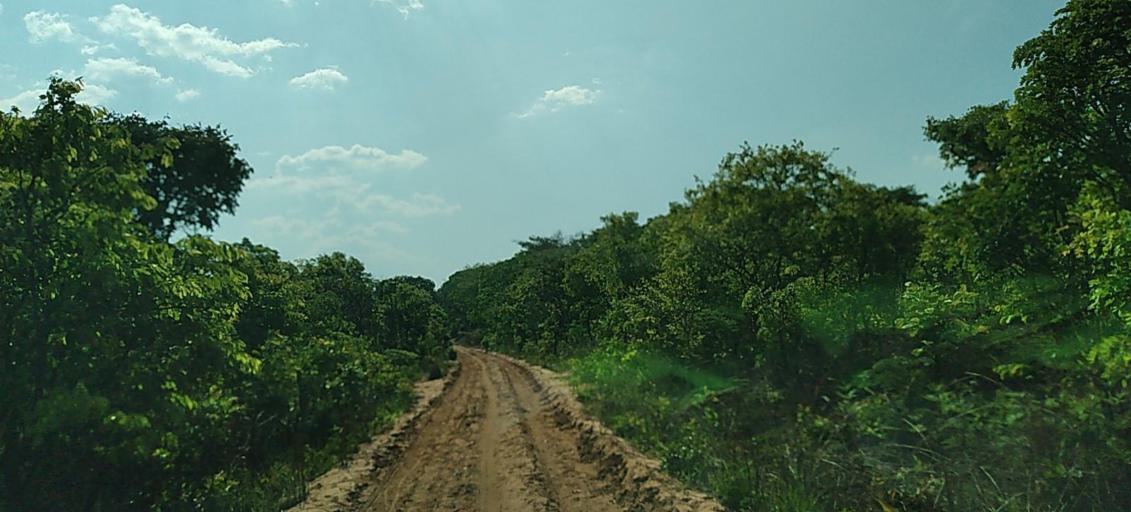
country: ZM
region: North-Western
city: Mwinilunga
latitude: -11.3008
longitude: 24.8726
